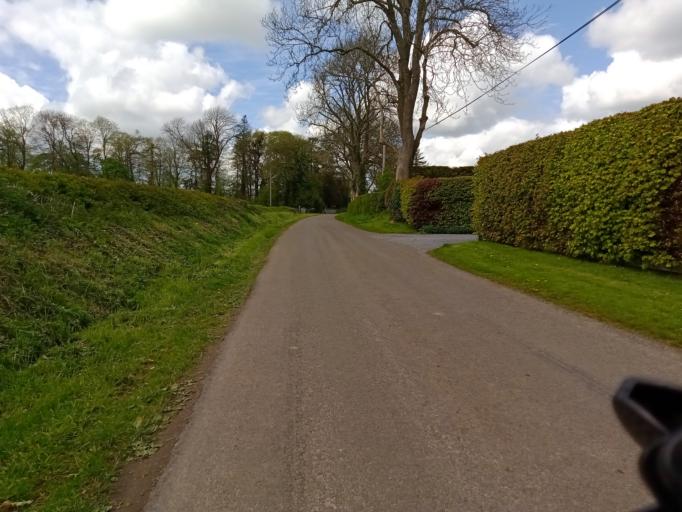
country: IE
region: Leinster
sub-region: Kilkenny
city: Thomastown
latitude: 52.5846
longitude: -7.1380
